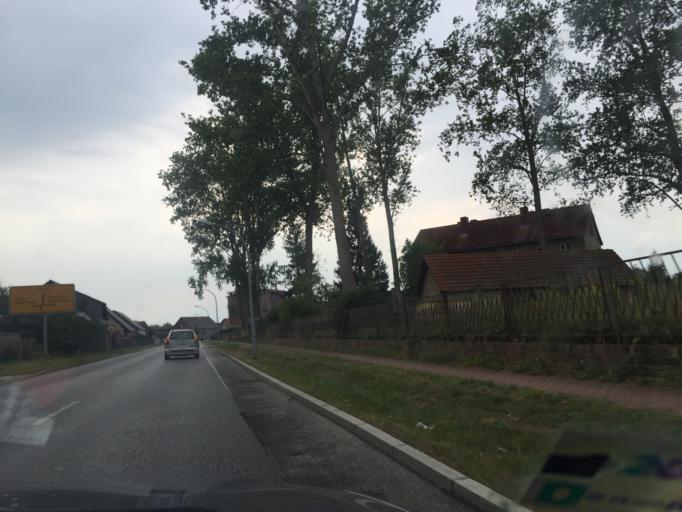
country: DE
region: Brandenburg
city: Wandlitz
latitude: 52.7865
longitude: 13.3947
